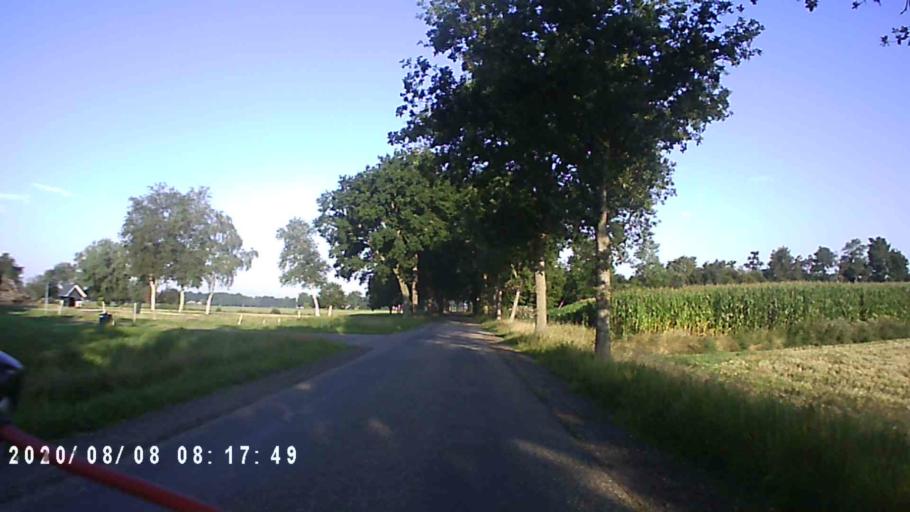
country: NL
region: Groningen
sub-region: Gemeente Leek
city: Leek
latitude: 53.0959
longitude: 6.3274
